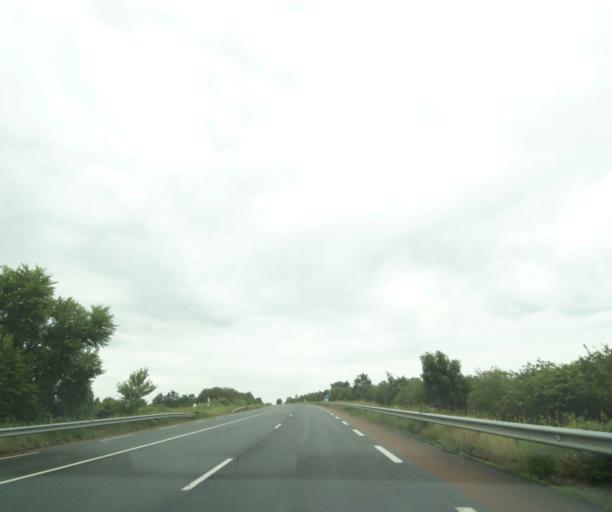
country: FR
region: Poitou-Charentes
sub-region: Departement des Deux-Sevres
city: Viennay
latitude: 46.7562
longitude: -0.2228
